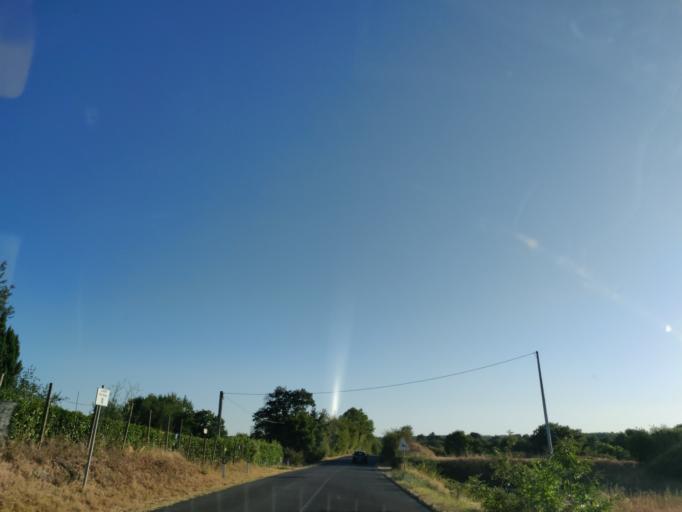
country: IT
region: Latium
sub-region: Provincia di Viterbo
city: Grotte di Castro
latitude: 42.6659
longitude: 11.8556
